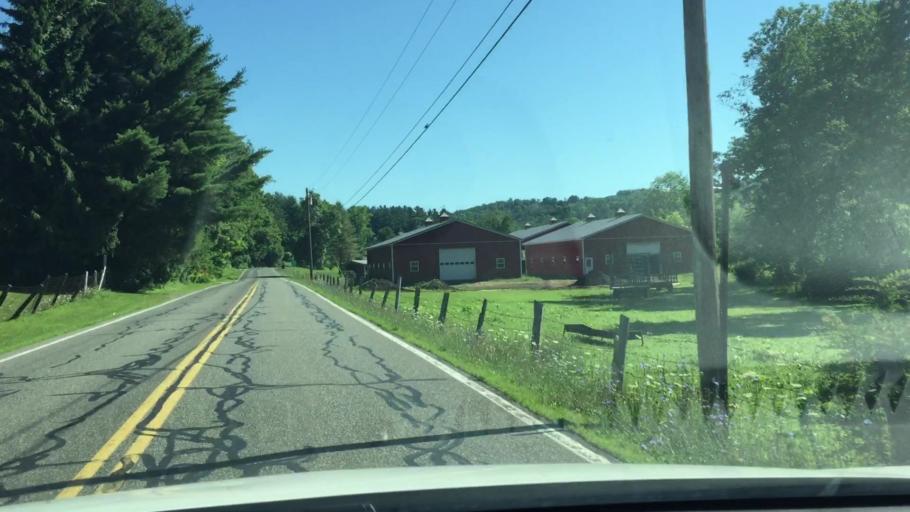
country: US
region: Massachusetts
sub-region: Berkshire County
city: West Stockbridge
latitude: 42.3506
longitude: -73.3626
